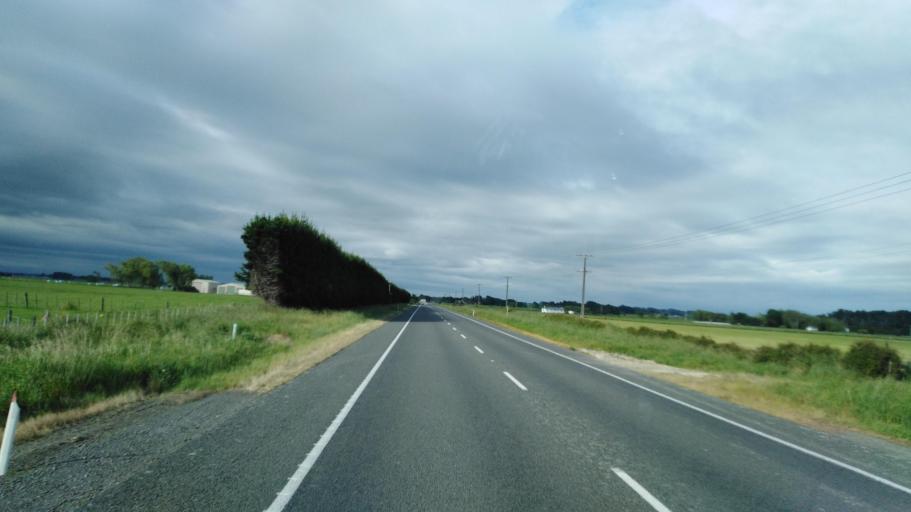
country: NZ
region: Manawatu-Wanganui
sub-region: Rangitikei District
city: Bulls
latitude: -40.2448
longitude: 175.4009
